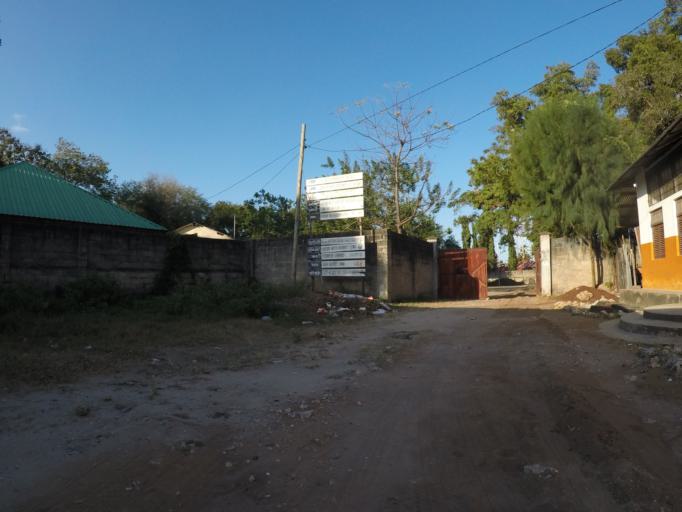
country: TZ
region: Zanzibar Urban/West
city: Zanzibar
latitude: -6.1714
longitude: 39.1994
